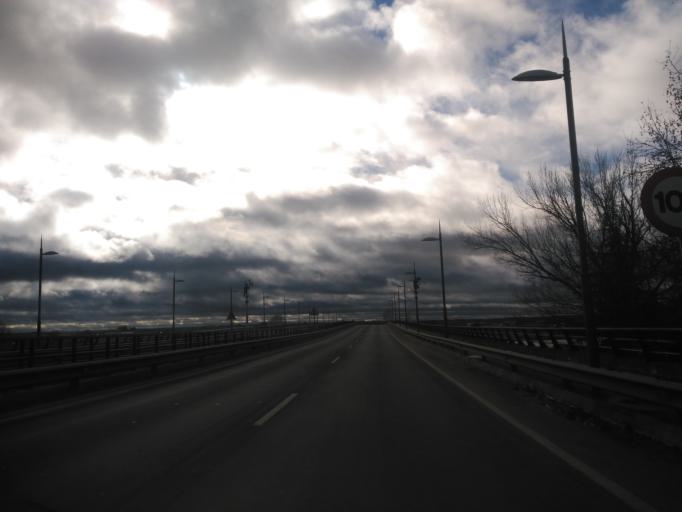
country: ES
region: Castille and Leon
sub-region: Provincia de Zamora
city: Zamora
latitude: 41.5038
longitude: -5.7315
